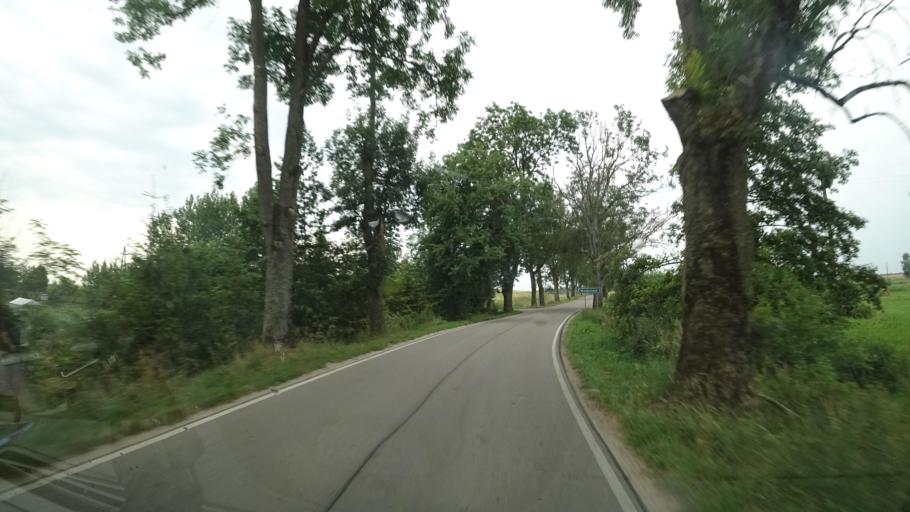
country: PL
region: Warmian-Masurian Voivodeship
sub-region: Powiat mragowski
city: Mikolajki
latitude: 53.8744
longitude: 21.5945
